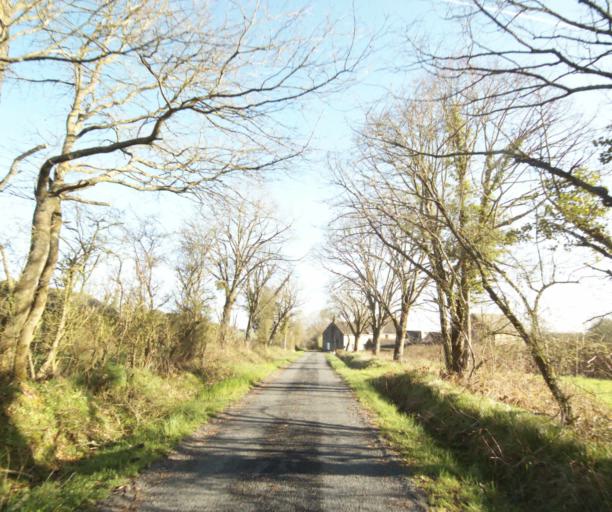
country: FR
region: Pays de la Loire
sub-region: Departement de la Loire-Atlantique
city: Fay-de-Bretagne
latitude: 47.4147
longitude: -1.8189
